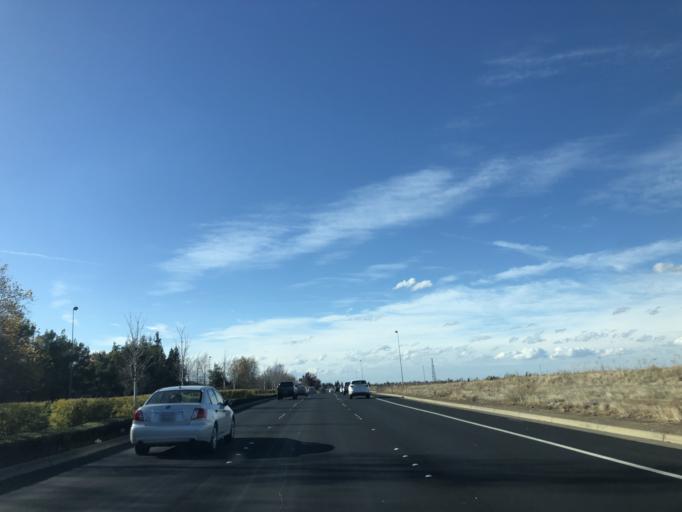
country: US
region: California
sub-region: Placer County
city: Roseville
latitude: 38.7776
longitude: -121.2820
